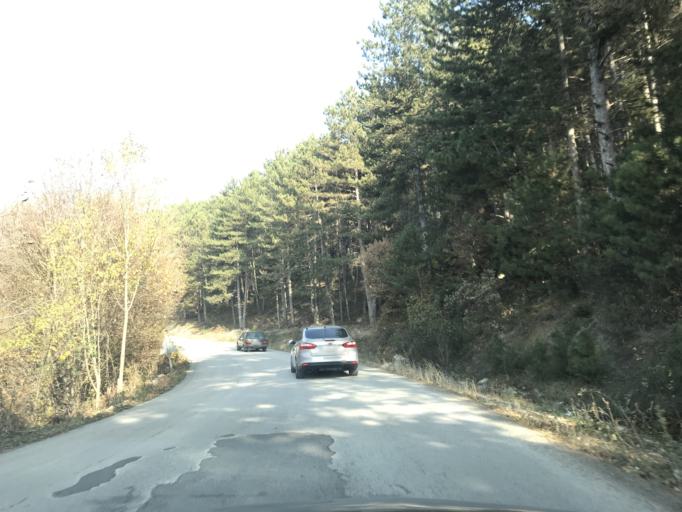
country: TR
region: Bolu
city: Bolu
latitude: 40.7810
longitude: 31.6324
